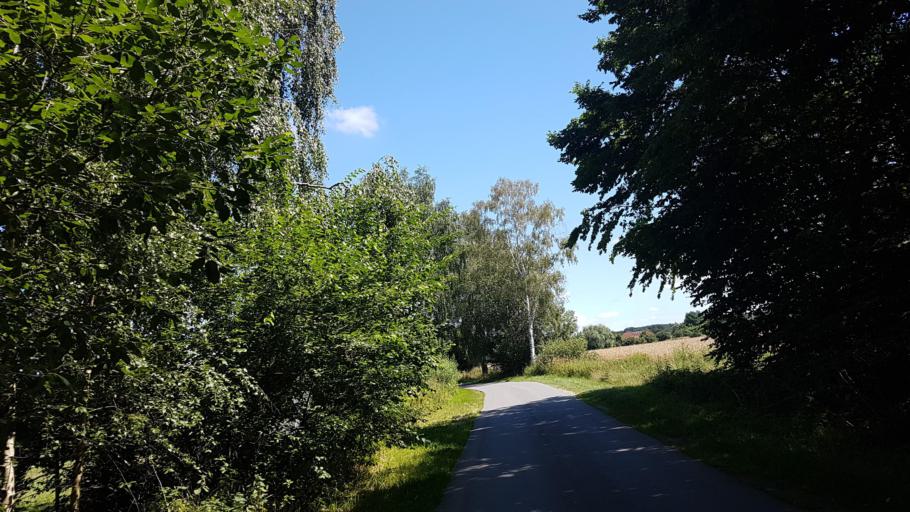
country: DE
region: Lower Saxony
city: Rullstorf
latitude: 53.2849
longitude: 10.5233
